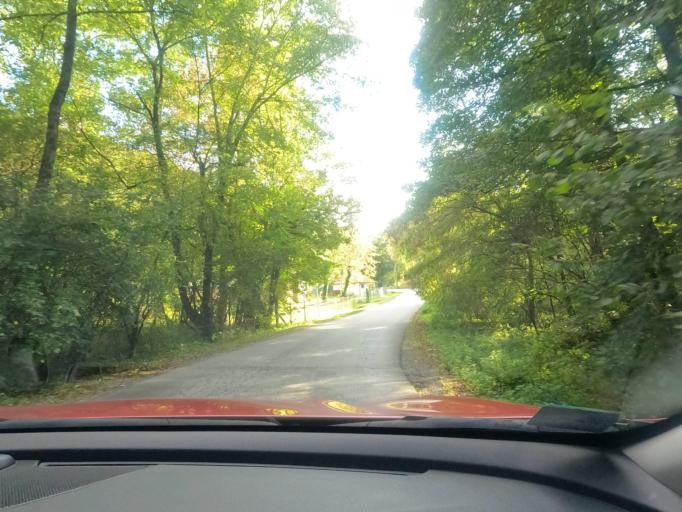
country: HR
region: Sisacko-Moslavacka
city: Petrinja
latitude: 45.3976
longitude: 16.2448
